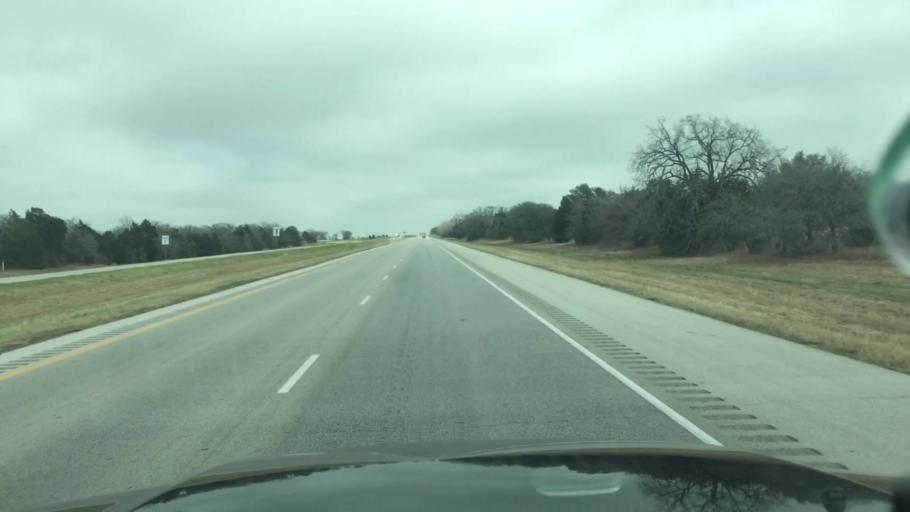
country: US
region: Texas
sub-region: Lee County
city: Giddings
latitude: 30.1407
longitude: -96.7606
